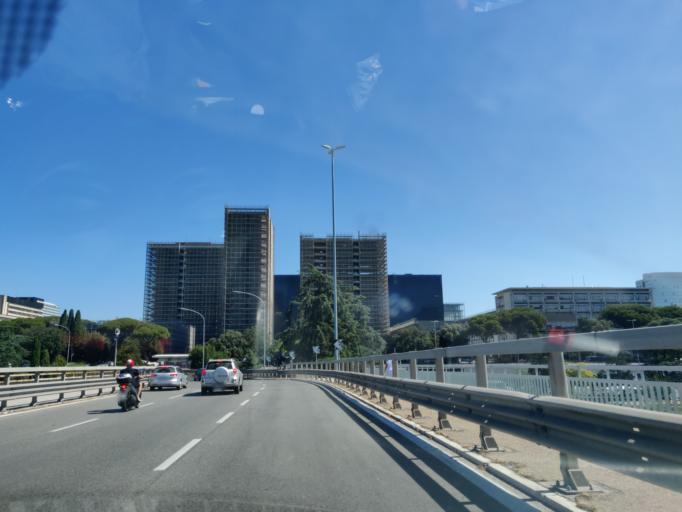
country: IT
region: Latium
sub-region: Citta metropolitana di Roma Capitale
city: Selcetta
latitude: 41.8276
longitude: 12.4696
